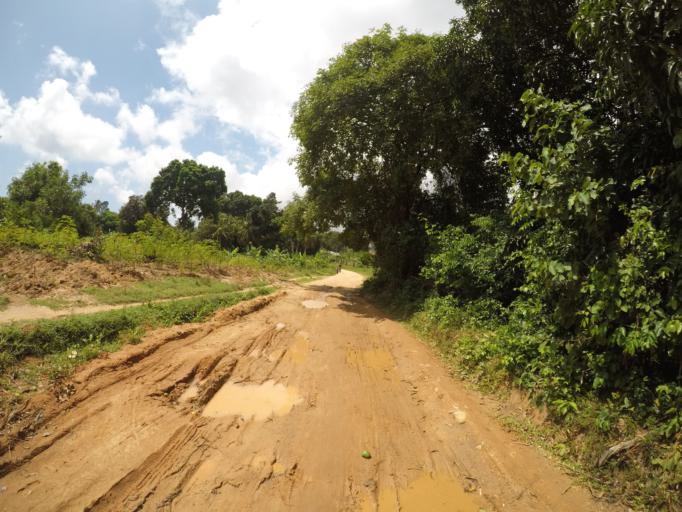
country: TZ
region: Pemba South
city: Mtambile
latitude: -5.3892
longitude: 39.7394
